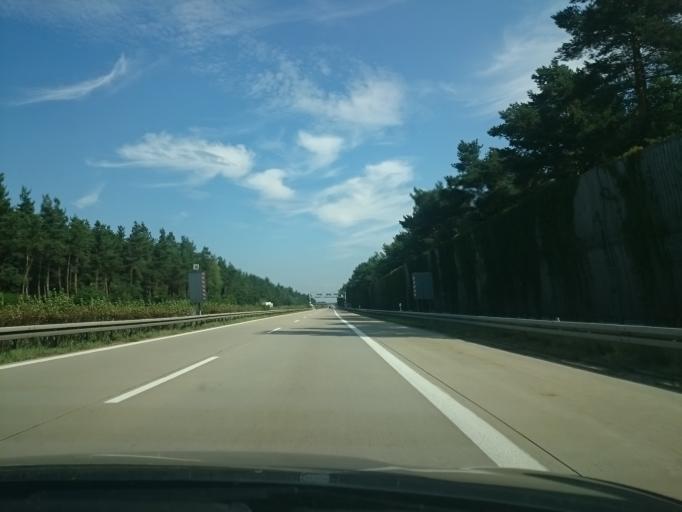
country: DE
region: Brandenburg
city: Ruhland
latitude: 51.4502
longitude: 13.8435
